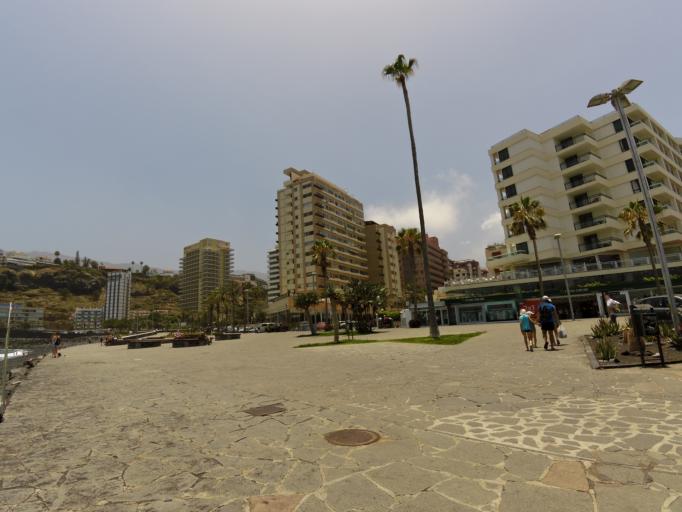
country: ES
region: Canary Islands
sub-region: Provincia de Santa Cruz de Tenerife
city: Puerto de la Cruz
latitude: 28.4191
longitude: -16.5420
